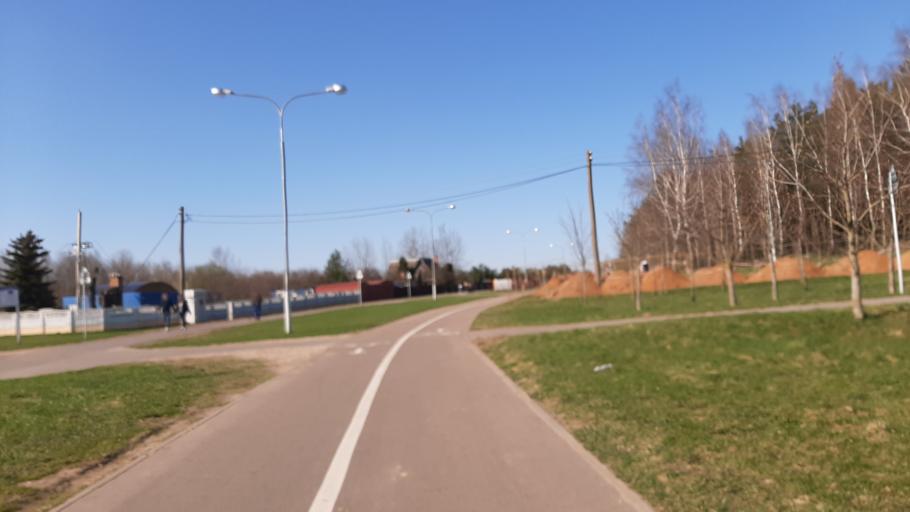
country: BY
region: Minsk
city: Bal'shavik
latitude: 53.9566
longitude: 27.5862
